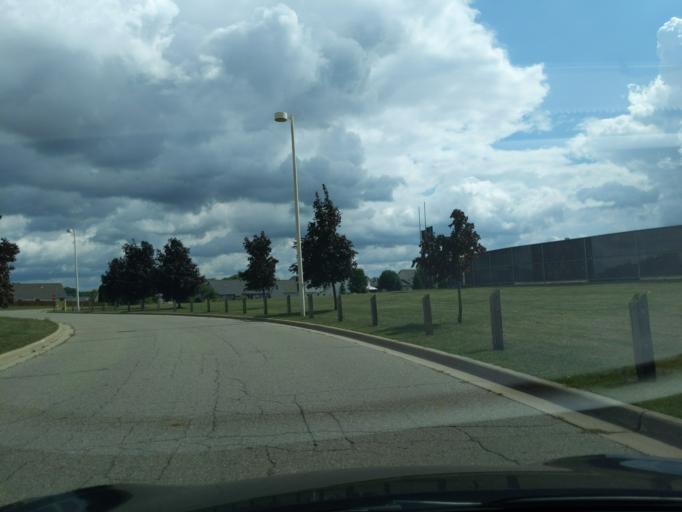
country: US
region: Michigan
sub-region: Ingham County
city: Holt
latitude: 42.6366
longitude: -84.5737
